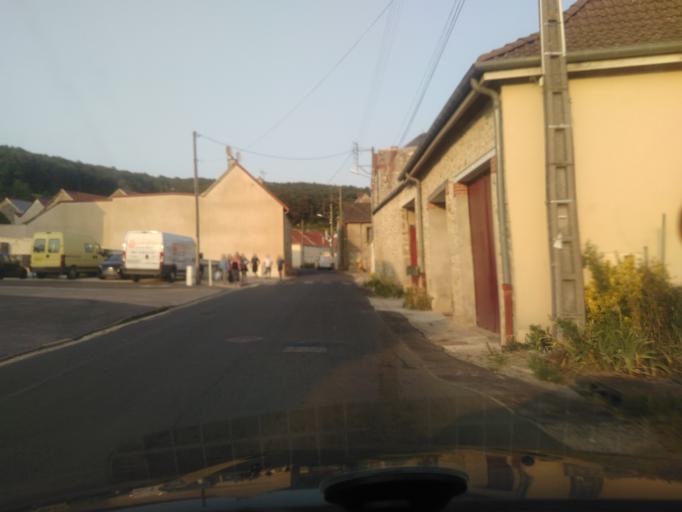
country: FR
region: Champagne-Ardenne
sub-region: Departement de la Marne
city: Damery
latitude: 49.0858
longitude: 3.8295
